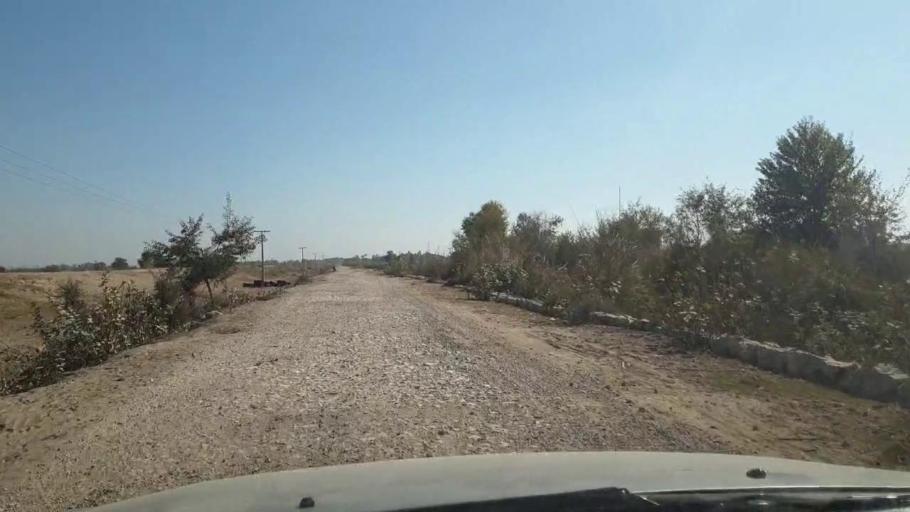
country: PK
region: Sindh
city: Ghotki
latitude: 28.0842
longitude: 69.3410
